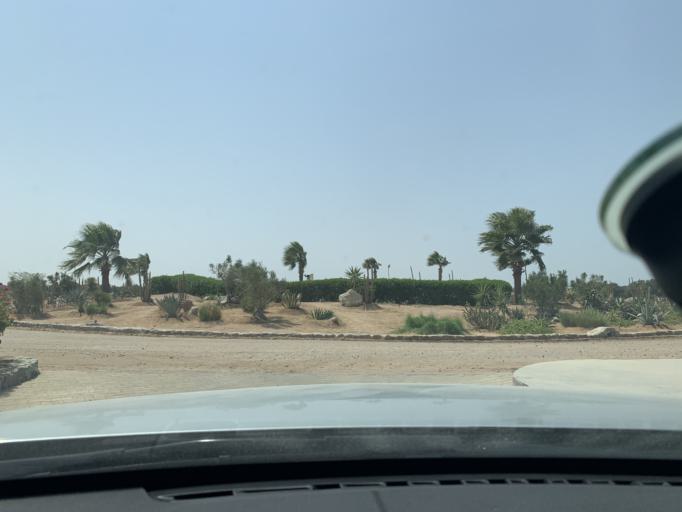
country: EG
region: Red Sea
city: El Gouna
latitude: 27.3822
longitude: 33.6608
